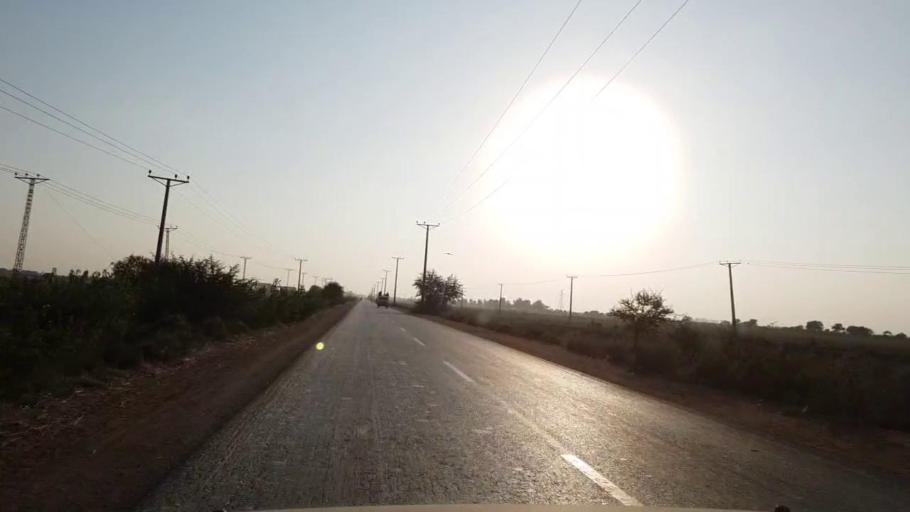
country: PK
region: Sindh
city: Daro Mehar
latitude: 24.6223
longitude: 68.0968
